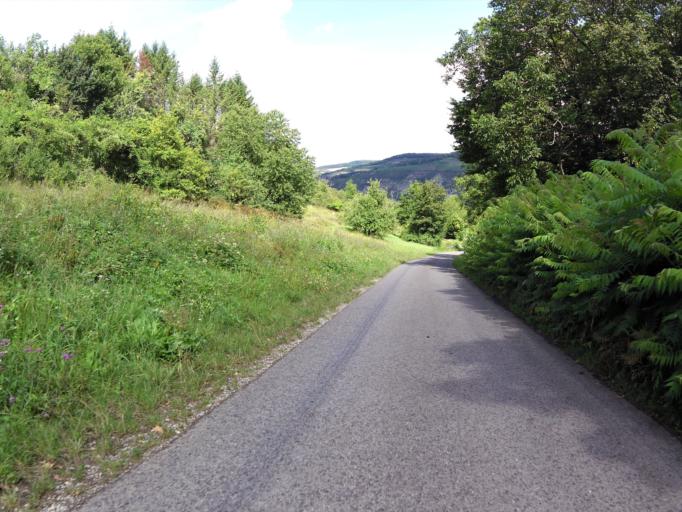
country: DE
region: Bavaria
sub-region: Regierungsbezirk Unterfranken
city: Margetshochheim
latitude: 49.8415
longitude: 9.8505
